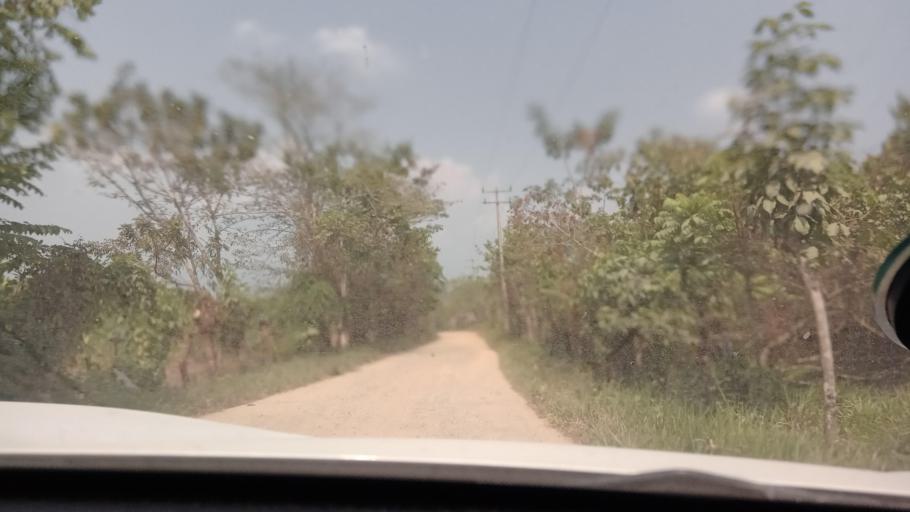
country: MX
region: Tabasco
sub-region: Huimanguillo
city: Francisco Rueda
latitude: 17.6767
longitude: -93.8641
